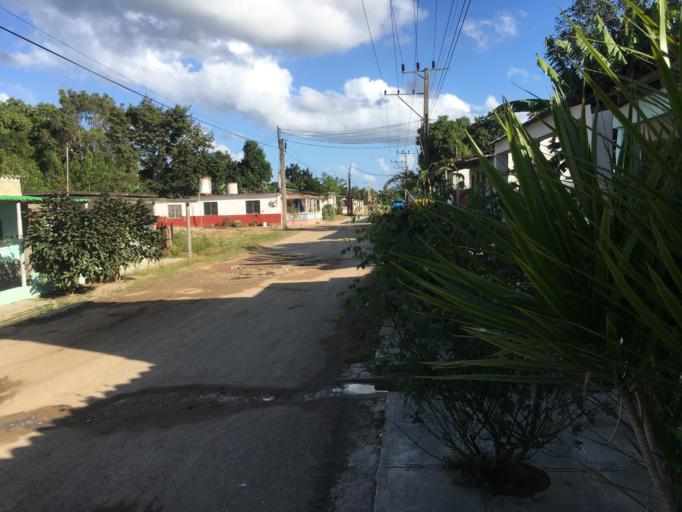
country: CU
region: Sancti Spiritus
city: Sancti Spiritus
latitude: 21.7426
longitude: -79.4642
